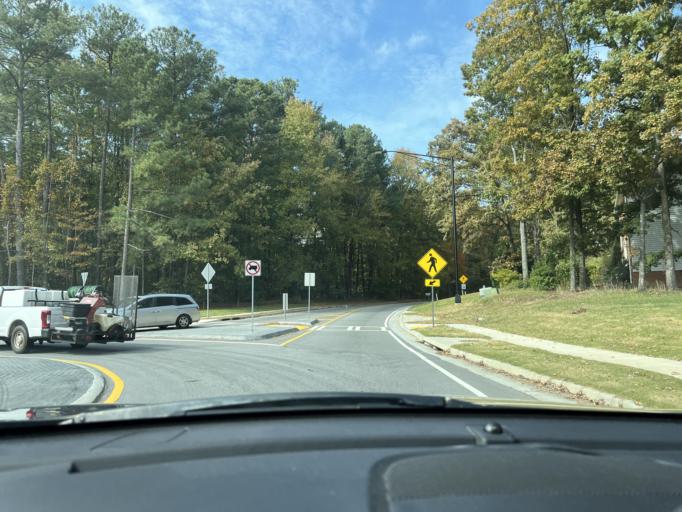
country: US
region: Georgia
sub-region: Gwinnett County
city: Snellville
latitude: 33.8827
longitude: -84.0023
